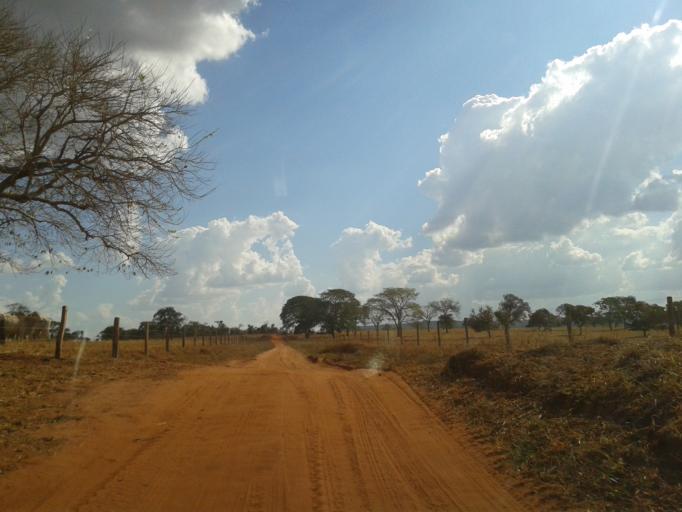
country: BR
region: Minas Gerais
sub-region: Santa Vitoria
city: Santa Vitoria
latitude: -19.2738
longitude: -49.9938
